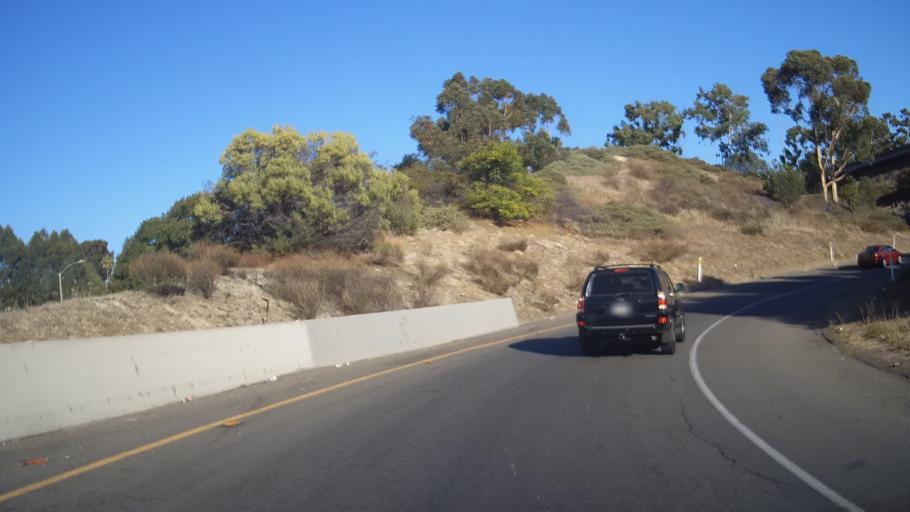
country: US
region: California
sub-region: San Diego County
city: La Mesa
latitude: 32.7794
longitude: -117.0031
